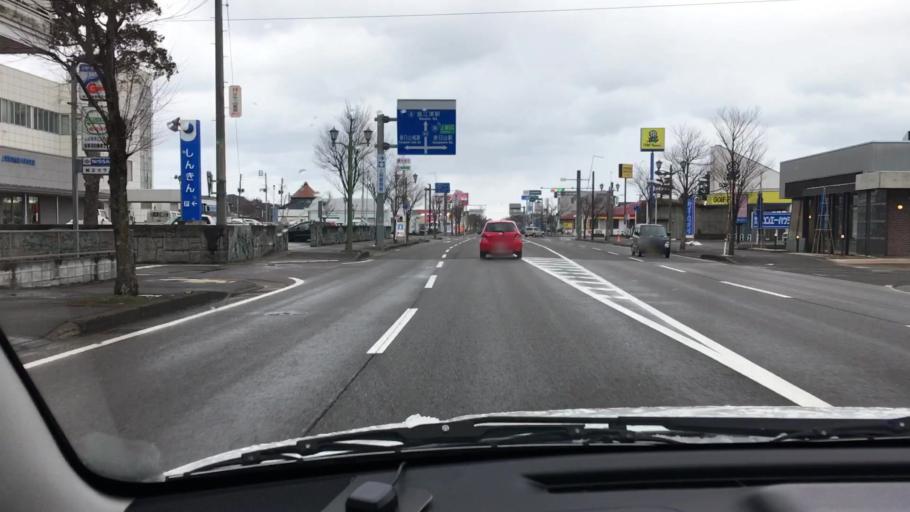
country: JP
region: Niigata
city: Joetsu
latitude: 37.1467
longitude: 138.2283
